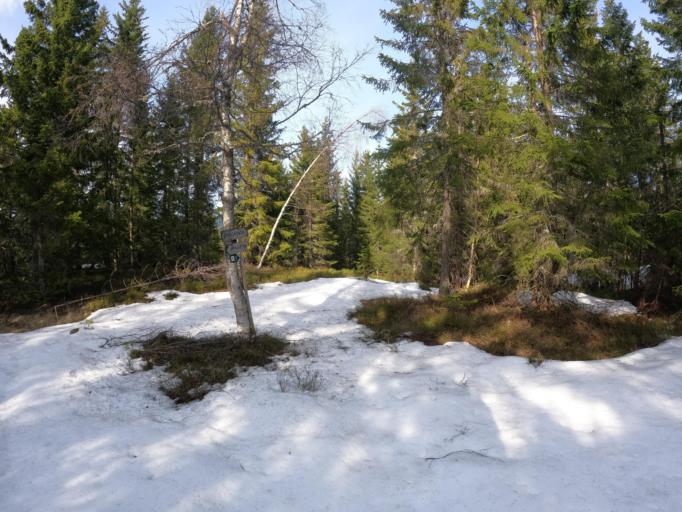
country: NO
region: Akershus
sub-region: Nannestad
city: Teigebyen
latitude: 60.2510
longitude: 10.8949
